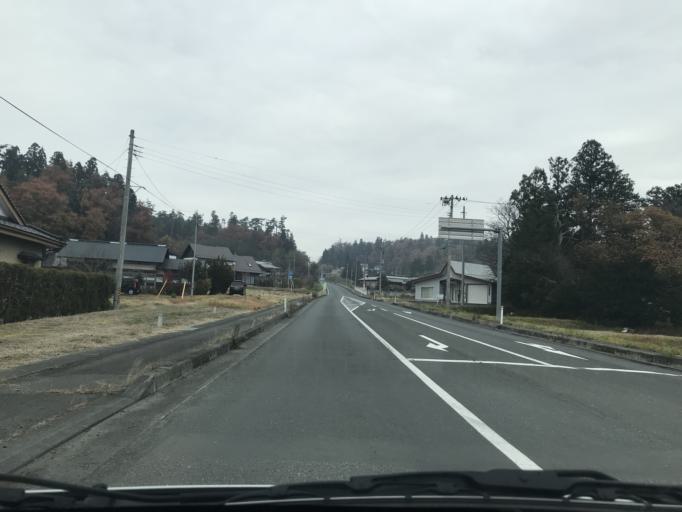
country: JP
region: Iwate
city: Mizusawa
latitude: 39.1608
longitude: 141.2011
